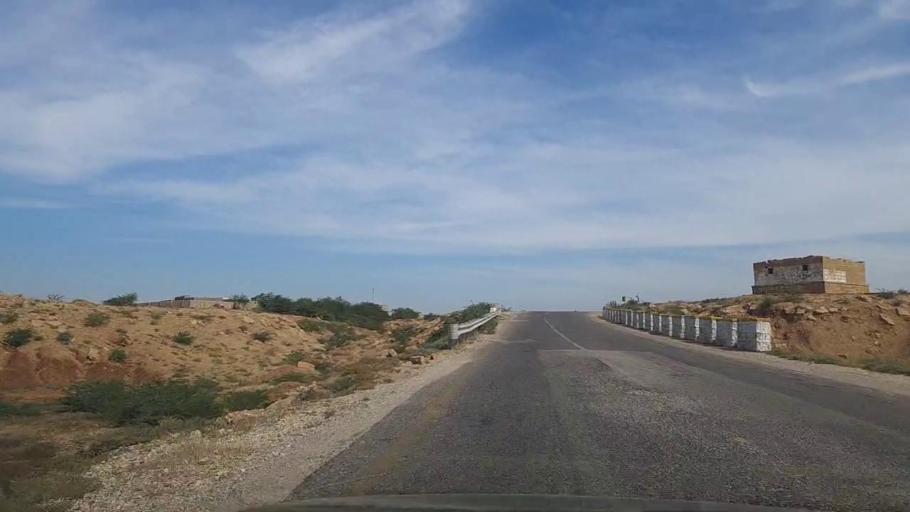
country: PK
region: Sindh
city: Daro Mehar
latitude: 24.9110
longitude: 68.0726
